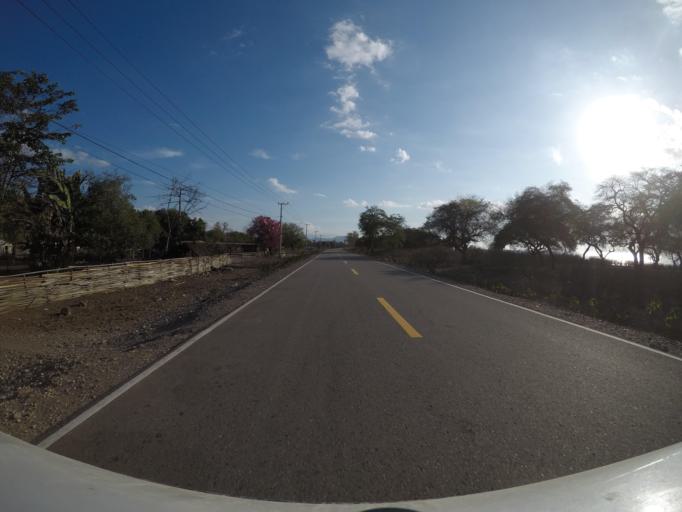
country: ID
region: East Nusa Tenggara
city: Atambua
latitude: -8.9263
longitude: 124.9866
